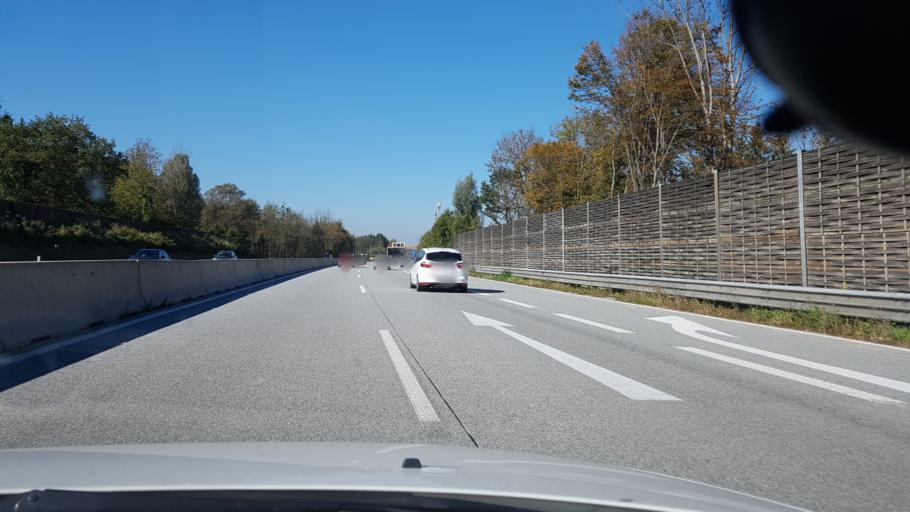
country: AT
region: Salzburg
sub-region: Politischer Bezirk Salzburg-Umgebung
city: Grodig
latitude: 47.7531
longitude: 13.0117
